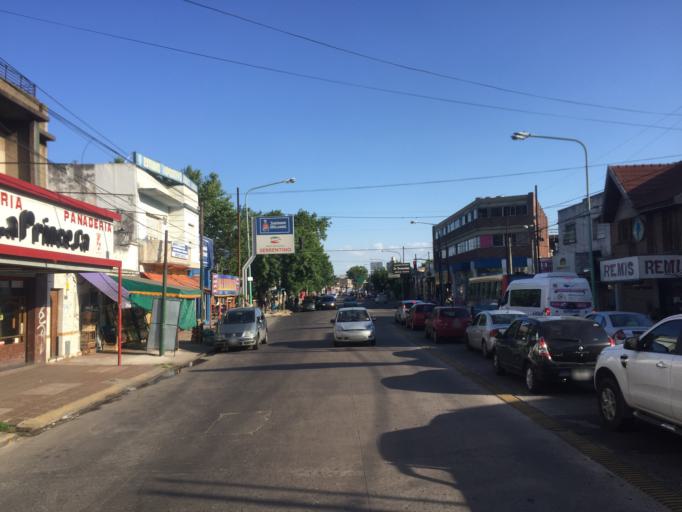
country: AR
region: Buenos Aires
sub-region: Partido de Lomas de Zamora
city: Lomas de Zamora
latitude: -34.7752
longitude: -58.3929
